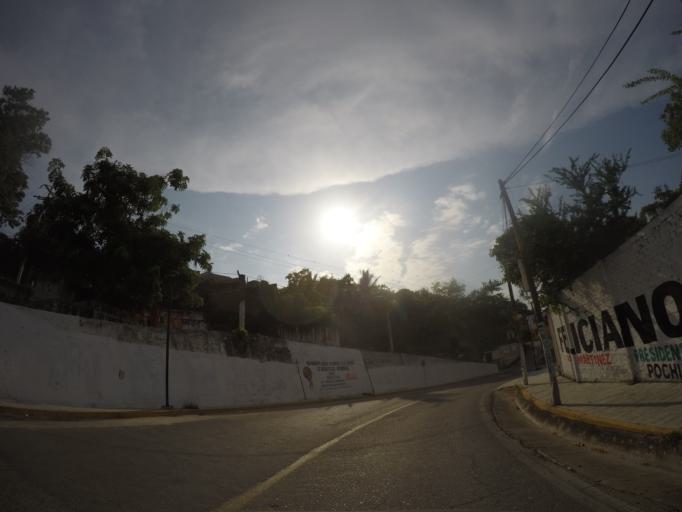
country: MX
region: Oaxaca
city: San Pedro Pochutla
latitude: 15.7509
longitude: -96.4667
